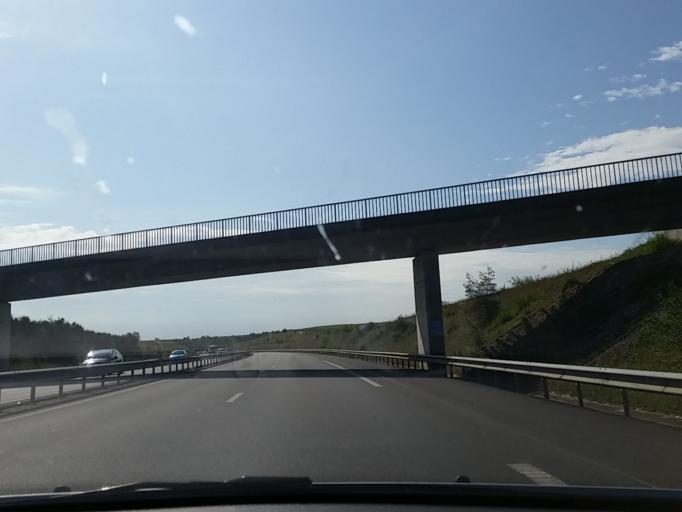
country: FR
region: Centre
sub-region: Departement du Cher
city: Trouy
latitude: 47.0107
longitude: 2.3864
